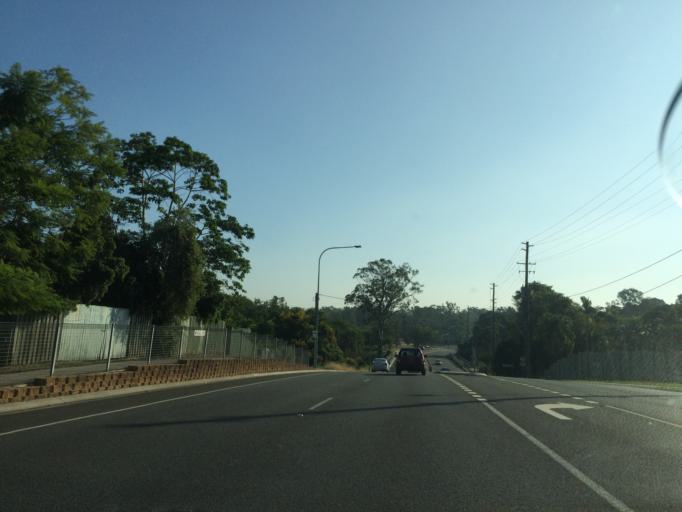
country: AU
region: Queensland
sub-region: Brisbane
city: Kenmore Hills
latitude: -27.5154
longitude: 152.9274
